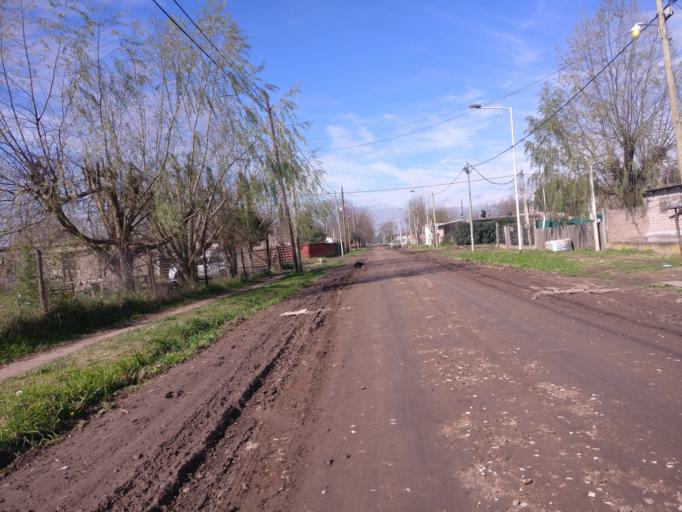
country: AR
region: Buenos Aires
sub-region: Partido de Ezeiza
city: Ezeiza
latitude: -34.9406
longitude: -58.6085
